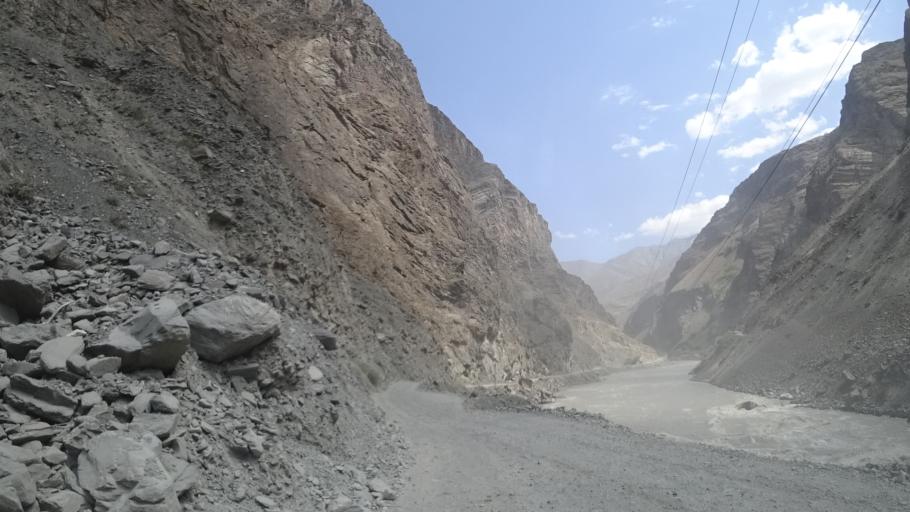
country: AF
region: Badakhshan
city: Maymay
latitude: 38.3415
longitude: 71.2000
